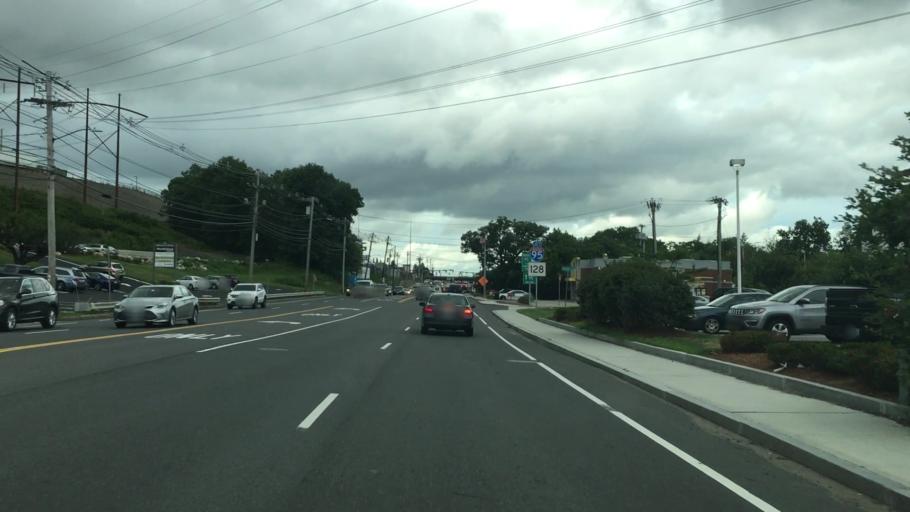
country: US
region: Massachusetts
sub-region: Middlesex County
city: Lexington
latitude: 42.4729
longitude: -71.2121
